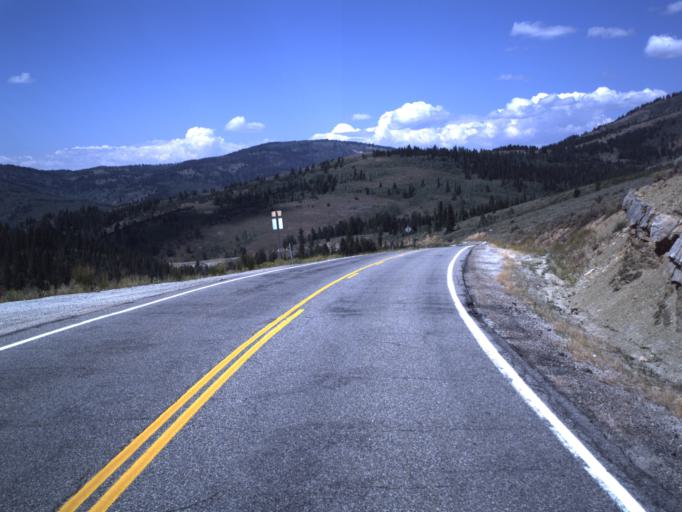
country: US
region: Idaho
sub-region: Bear Lake County
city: Paris
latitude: 41.9522
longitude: -111.4960
